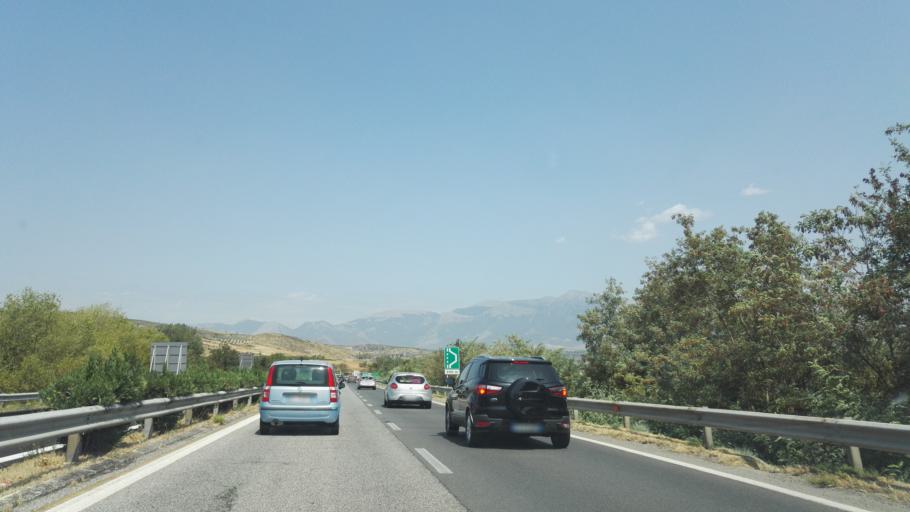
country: IT
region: Calabria
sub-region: Provincia di Cosenza
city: Firmo
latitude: 39.7296
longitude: 16.2349
